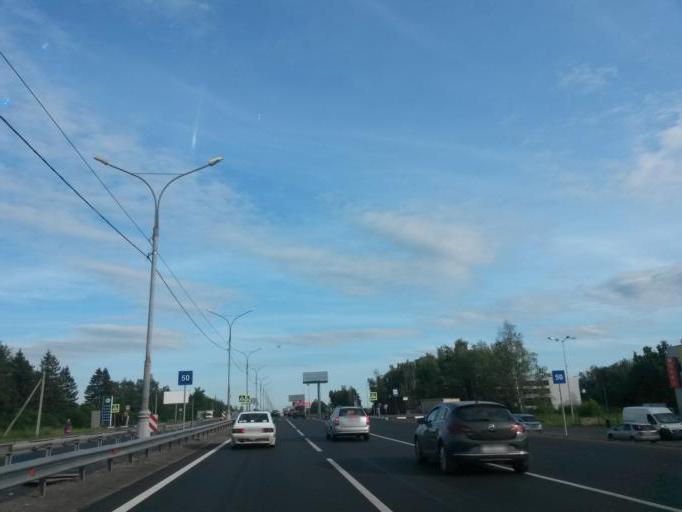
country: RU
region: Moskovskaya
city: Petrovskaya
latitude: 55.5335
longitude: 37.8115
